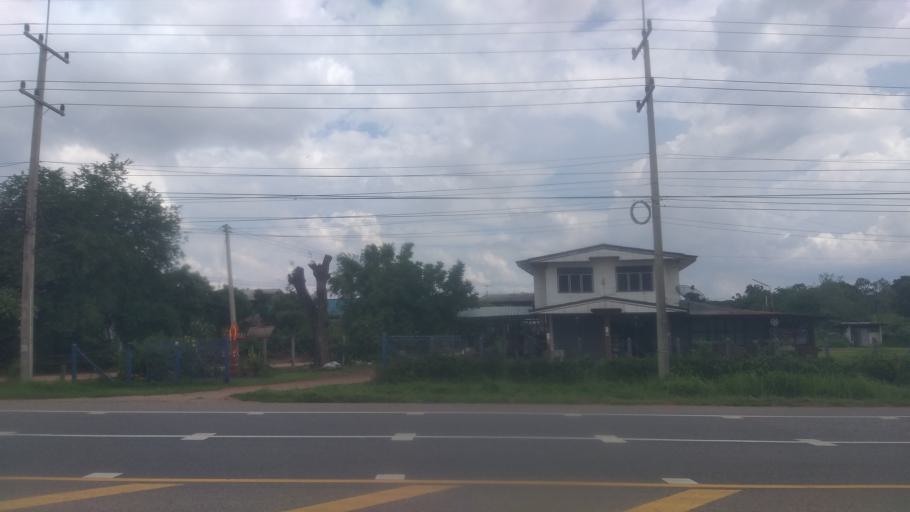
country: TH
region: Chaiyaphum
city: Noen Sa-nga
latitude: 15.6761
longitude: 101.9779
